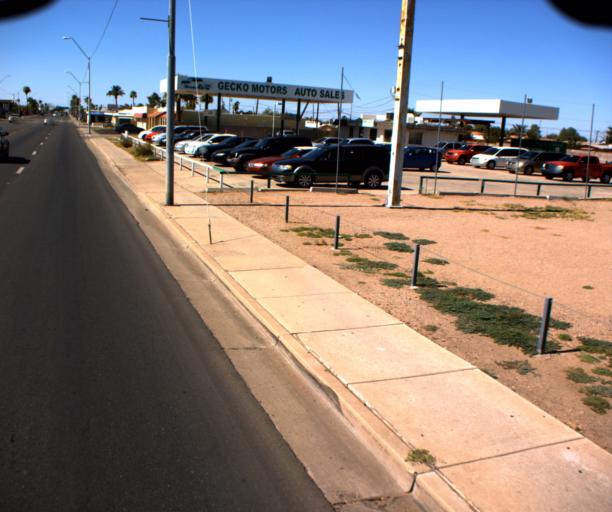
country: US
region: Arizona
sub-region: Pinal County
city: Casa Grande
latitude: 32.8867
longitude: -111.7574
